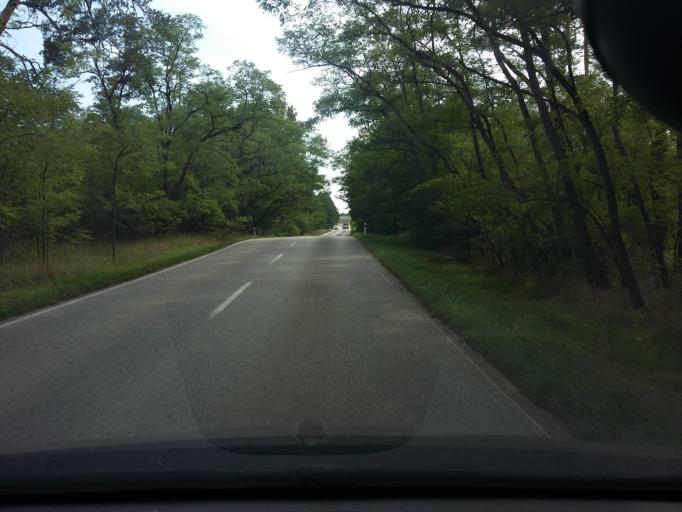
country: SK
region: Trnavsky
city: Gbely
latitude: 48.5917
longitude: 17.1862
